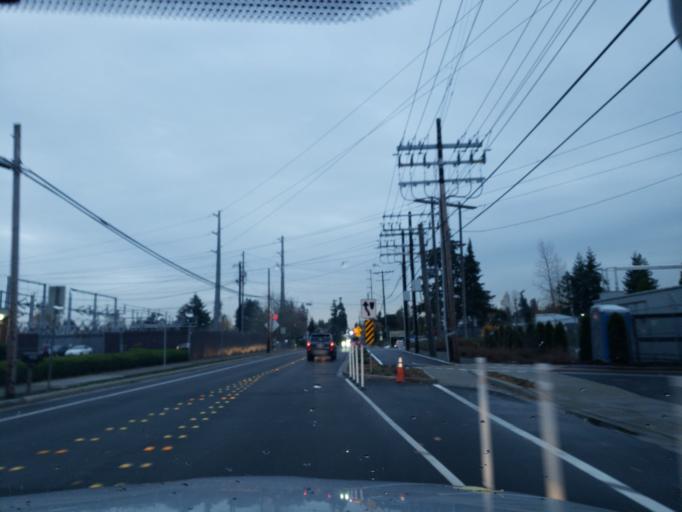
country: US
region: Washington
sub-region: Snohomish County
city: Lynnwood
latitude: 47.8067
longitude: -122.3159
